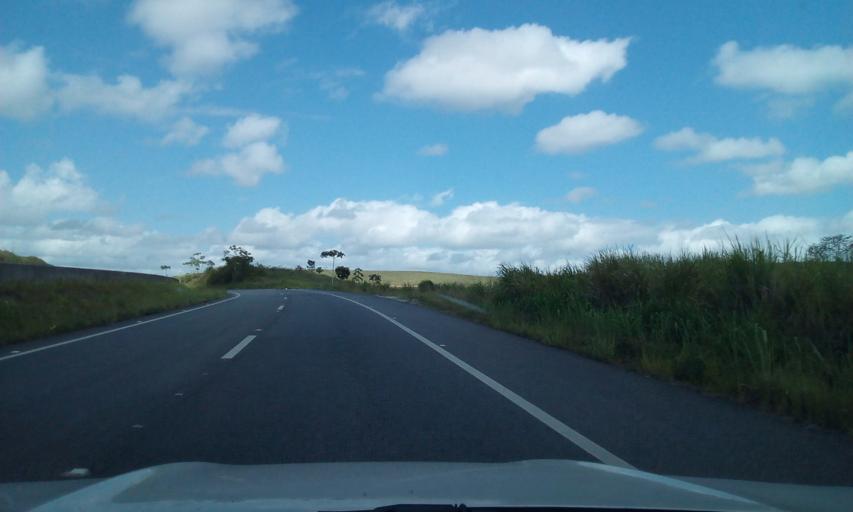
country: BR
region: Alagoas
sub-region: Rio Largo
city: Rio Largo
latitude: -9.4897
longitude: -35.8970
